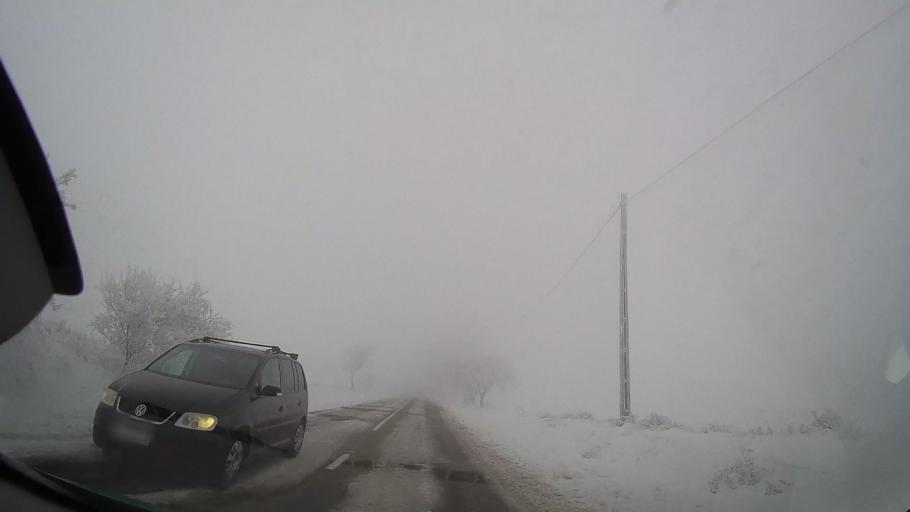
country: RO
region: Neamt
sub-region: Comuna Valea Ursului
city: Valea Ursului
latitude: 46.8041
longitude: 27.0722
